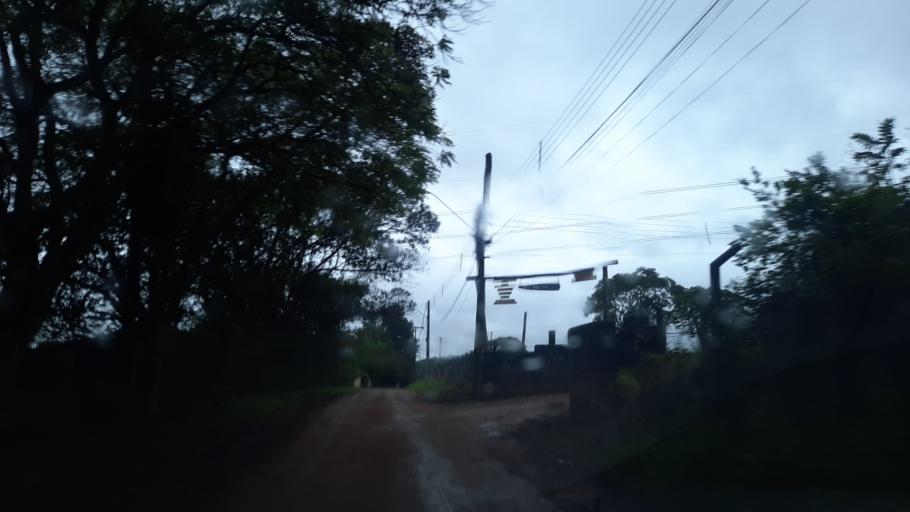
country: BR
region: Sao Paulo
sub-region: Atibaia
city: Atibaia
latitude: -23.0725
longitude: -46.5074
